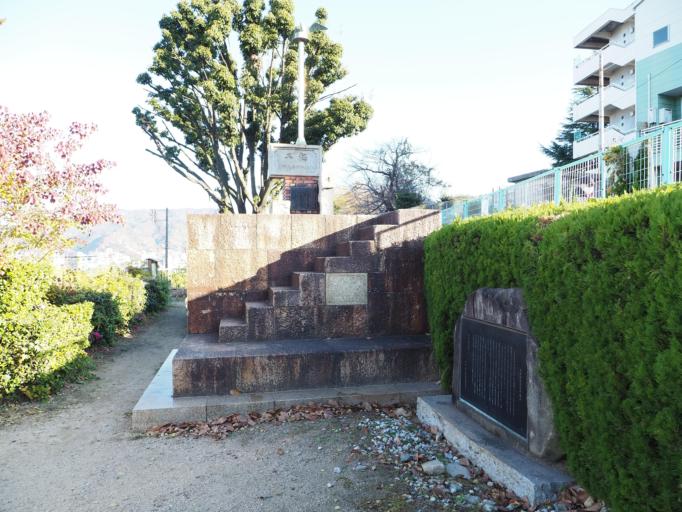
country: JP
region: Hiroshima
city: Kure
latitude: 34.2327
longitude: 132.5610
